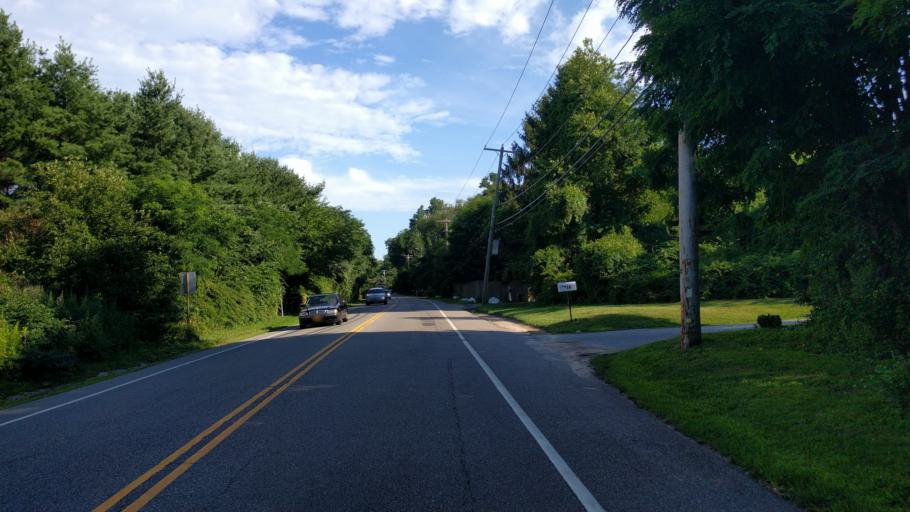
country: US
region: New York
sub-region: Nassau County
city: Oyster Bay Cove
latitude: 40.8564
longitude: -73.5124
